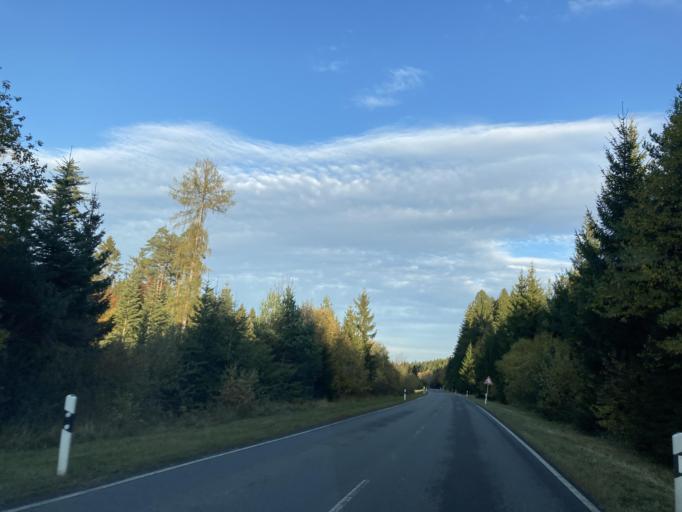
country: DE
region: Baden-Wuerttemberg
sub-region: Freiburg Region
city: Braunlingen
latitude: 48.0035
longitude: 8.4301
